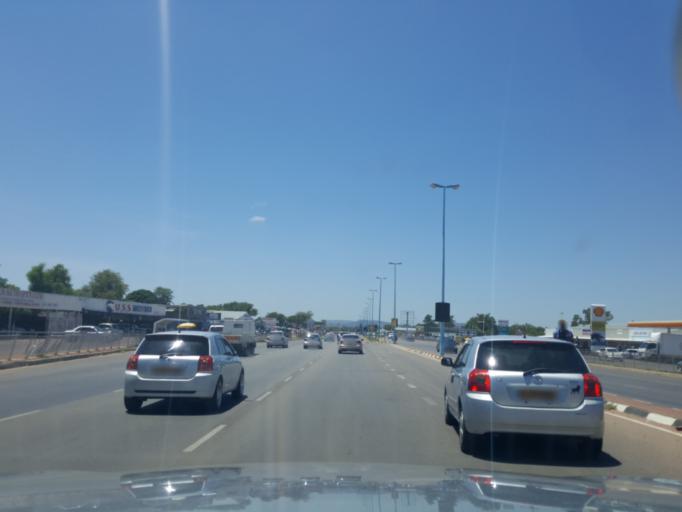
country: BW
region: Kweneng
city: Mogoditshane
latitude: -24.6255
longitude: 25.8697
